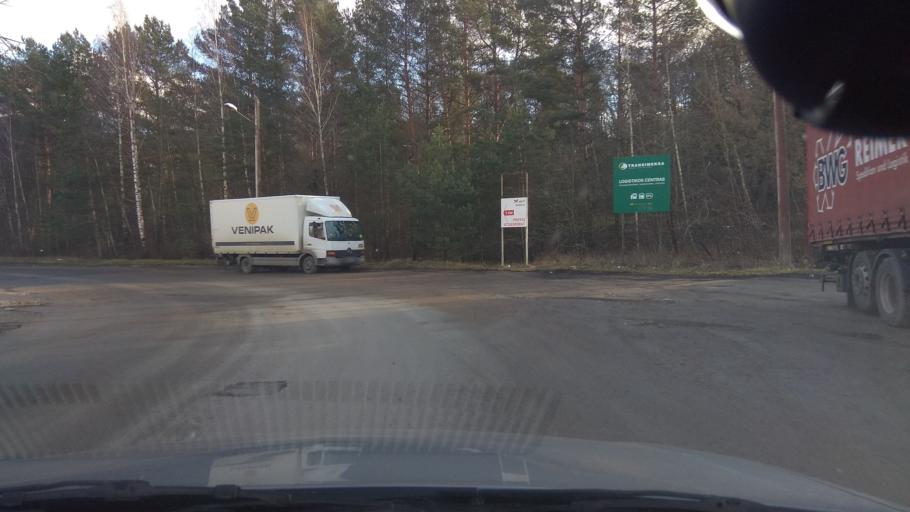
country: LT
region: Vilnius County
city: Lazdynai
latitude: 54.6451
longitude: 25.2141
